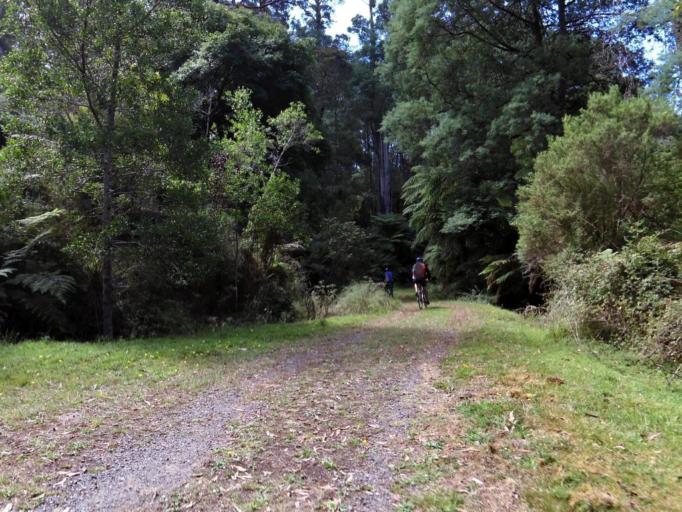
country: AU
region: Victoria
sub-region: Yarra Ranges
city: Millgrove
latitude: -37.7026
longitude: 145.7828
